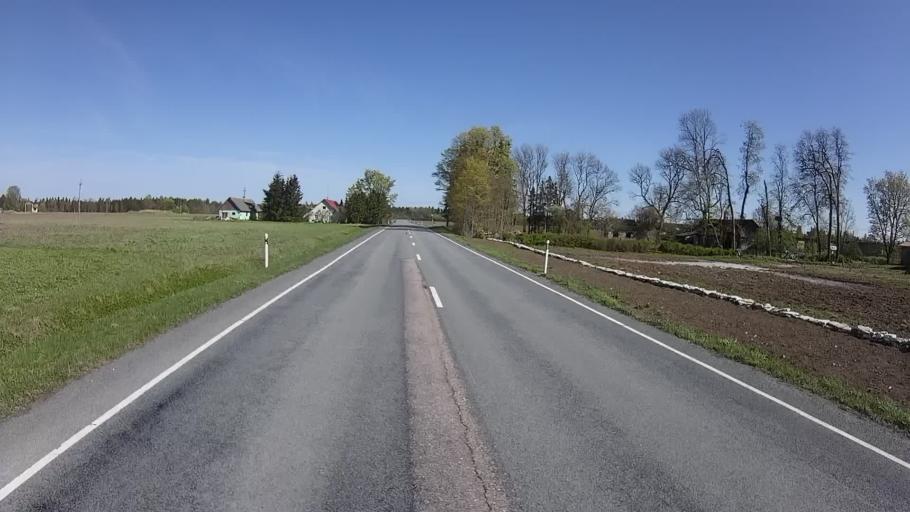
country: EE
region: Raplamaa
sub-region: Jaervakandi vald
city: Jarvakandi
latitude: 58.8413
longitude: 24.7966
